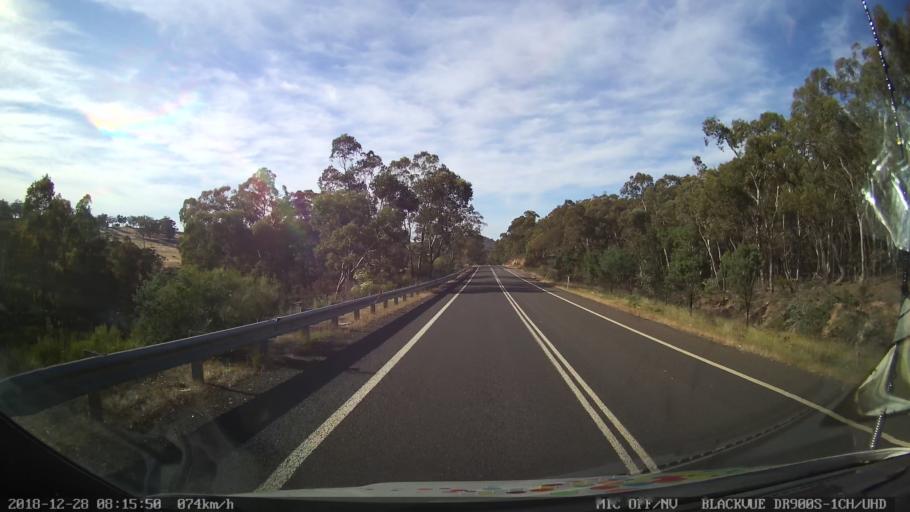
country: AU
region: New South Wales
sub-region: Blayney
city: Blayney
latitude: -33.8265
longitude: 149.3296
